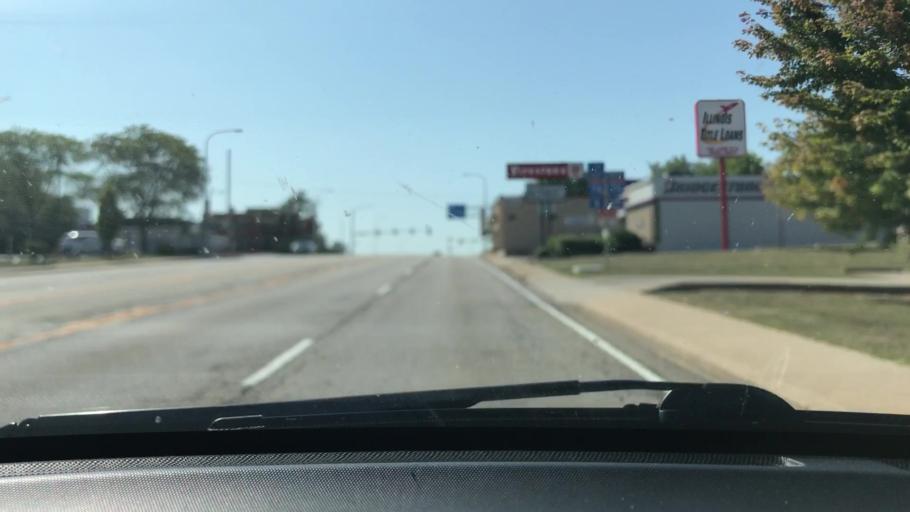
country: US
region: Illinois
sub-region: Peoria County
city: Peoria
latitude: 40.7070
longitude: -89.5941
